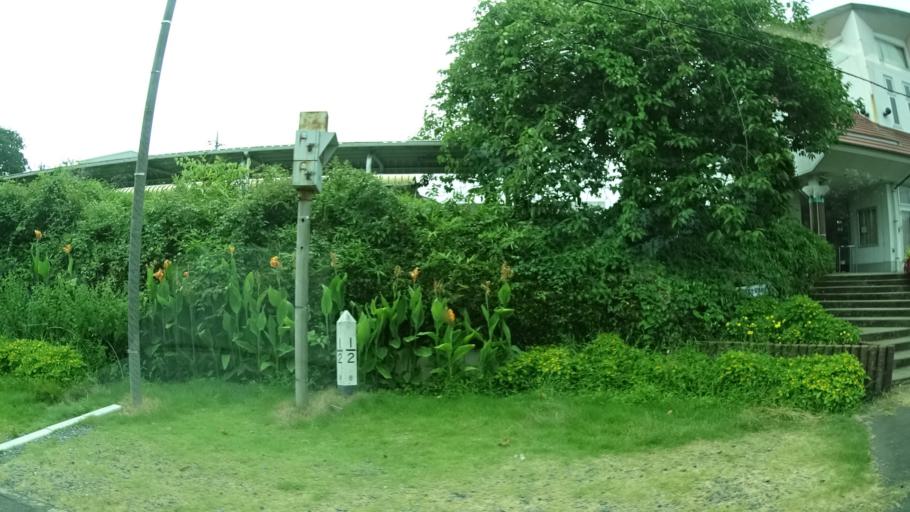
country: JP
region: Tochigi
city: Mooka
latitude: 36.3756
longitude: 139.9717
